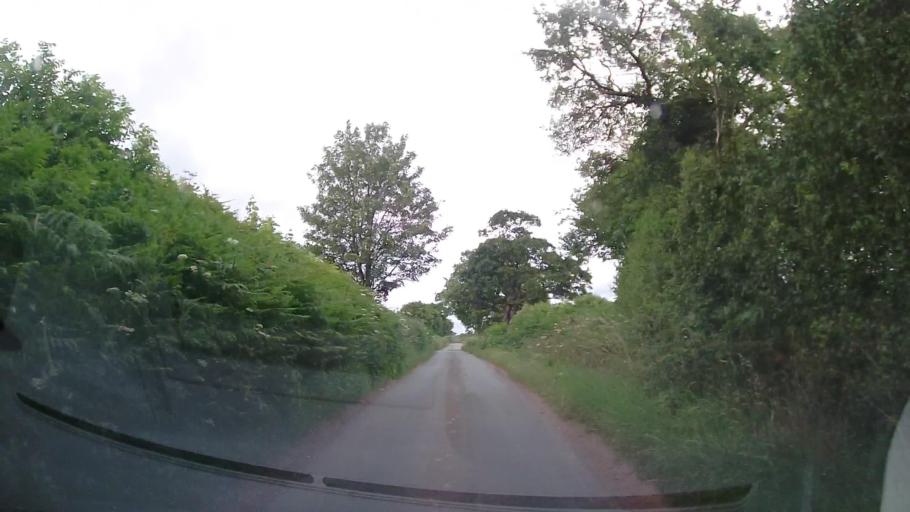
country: GB
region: England
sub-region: Shropshire
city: Whitchurch
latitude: 52.9327
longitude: -2.7300
